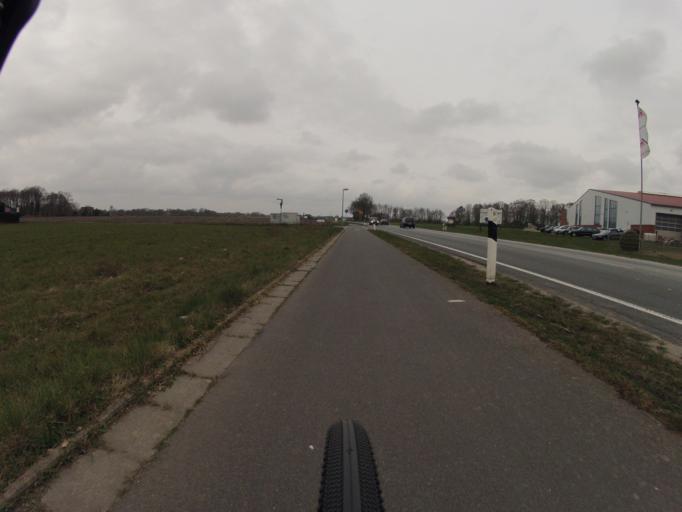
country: DE
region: North Rhine-Westphalia
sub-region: Regierungsbezirk Munster
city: Recke
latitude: 52.3400
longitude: 7.7385
